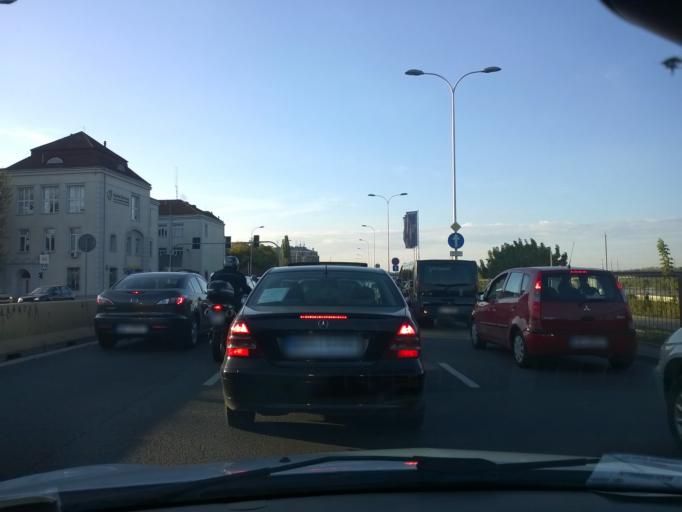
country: PL
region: Masovian Voivodeship
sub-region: Warszawa
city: Praga Polnoc
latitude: 52.2449
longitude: 21.0239
